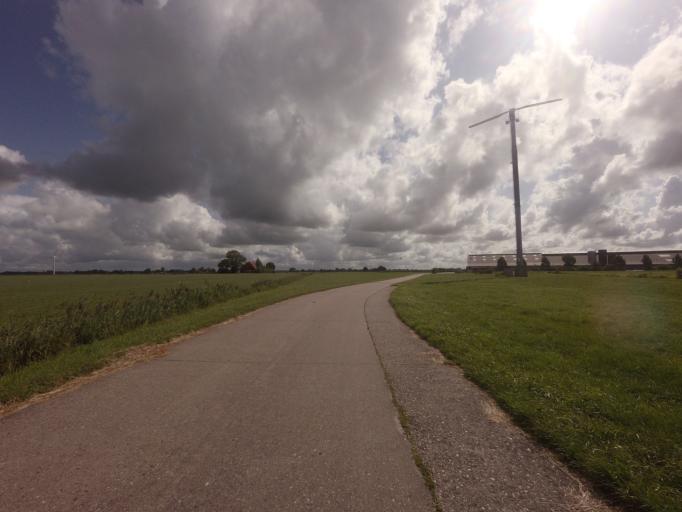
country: NL
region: Friesland
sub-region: Sudwest Fryslan
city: Scharnegoutum
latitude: 53.0731
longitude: 5.6371
